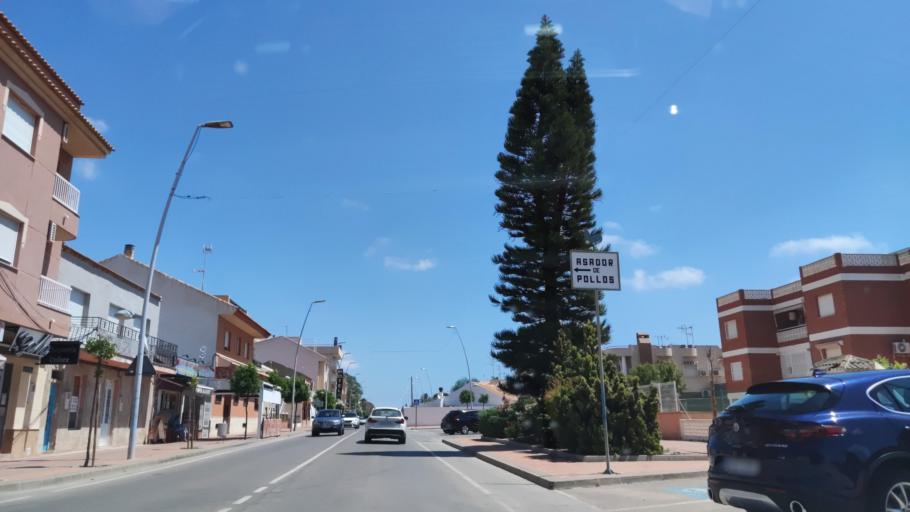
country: ES
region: Murcia
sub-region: Murcia
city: Los Alcazares
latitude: 37.7564
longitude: -0.8405
